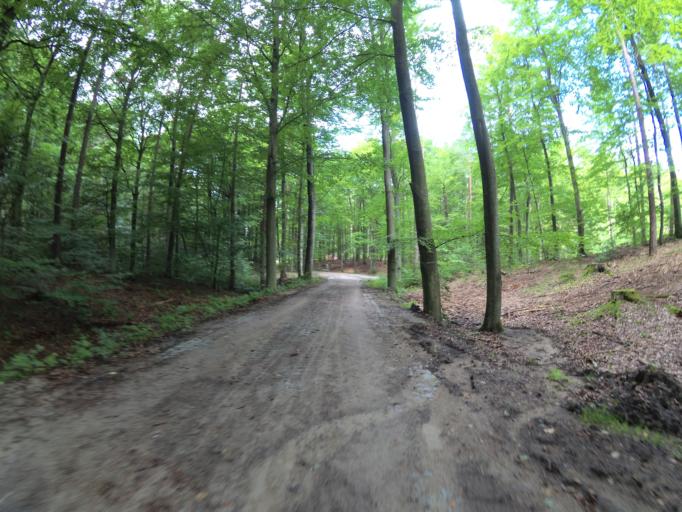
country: PL
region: Pomeranian Voivodeship
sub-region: Powiat wejherowski
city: Bojano
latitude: 54.5068
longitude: 18.4187
